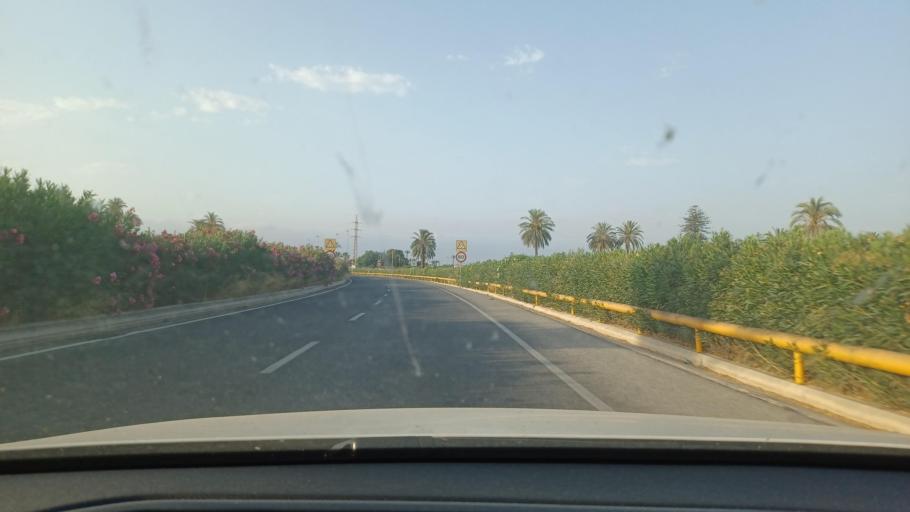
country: ES
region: Valencia
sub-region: Provincia de Alicante
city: Elche
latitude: 38.2343
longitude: -0.7004
